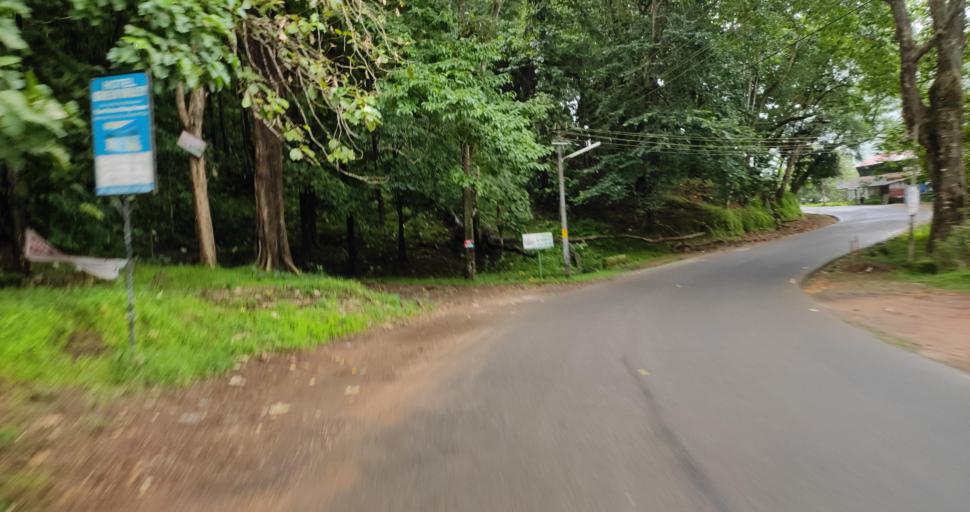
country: IN
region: Kerala
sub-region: Ernakulam
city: Angamali
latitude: 10.2892
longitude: 76.5622
